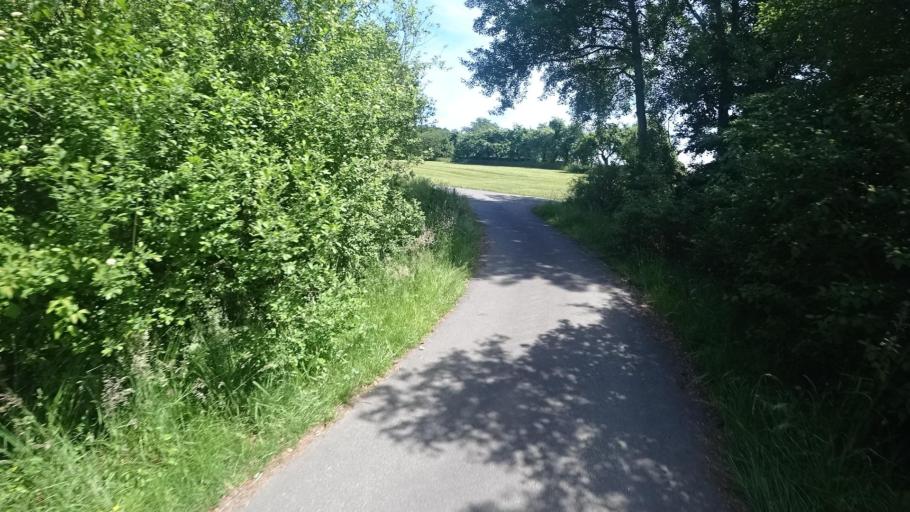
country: DE
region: Rheinland-Pfalz
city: Mammelzen
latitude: 50.6976
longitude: 7.6678
